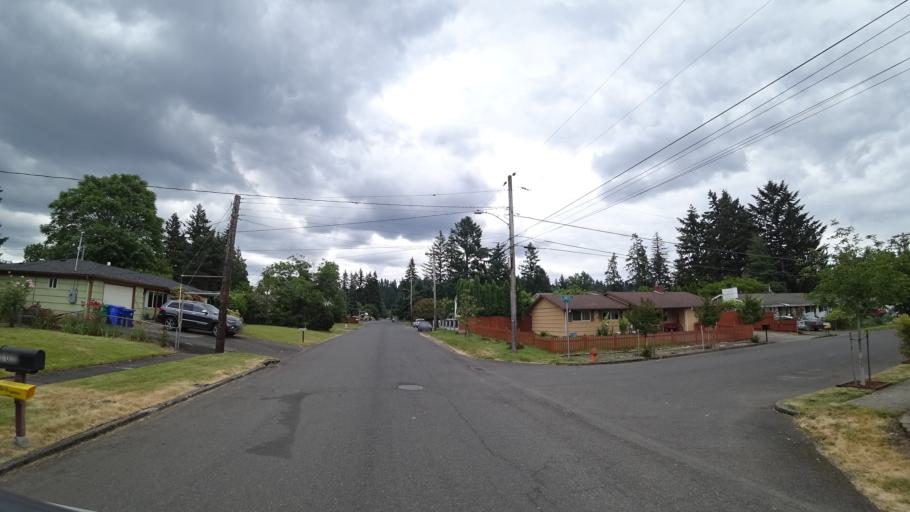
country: US
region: Oregon
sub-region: Clackamas County
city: Happy Valley
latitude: 45.5002
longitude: -122.4990
